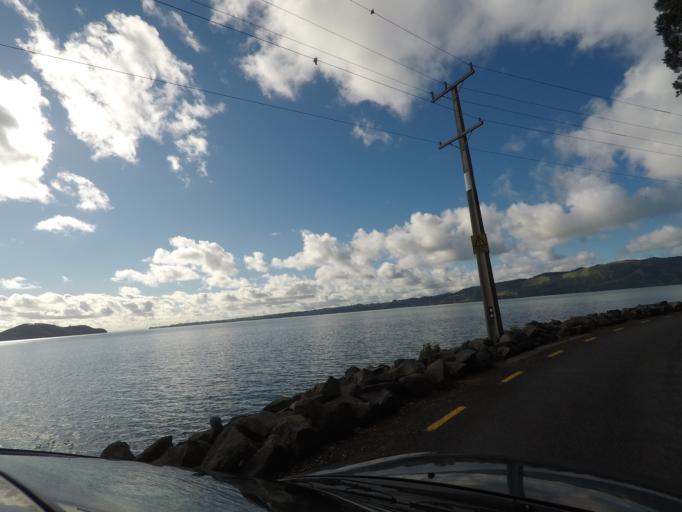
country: NZ
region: Auckland
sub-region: Auckland
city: Titirangi
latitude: -37.0104
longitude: 174.5625
